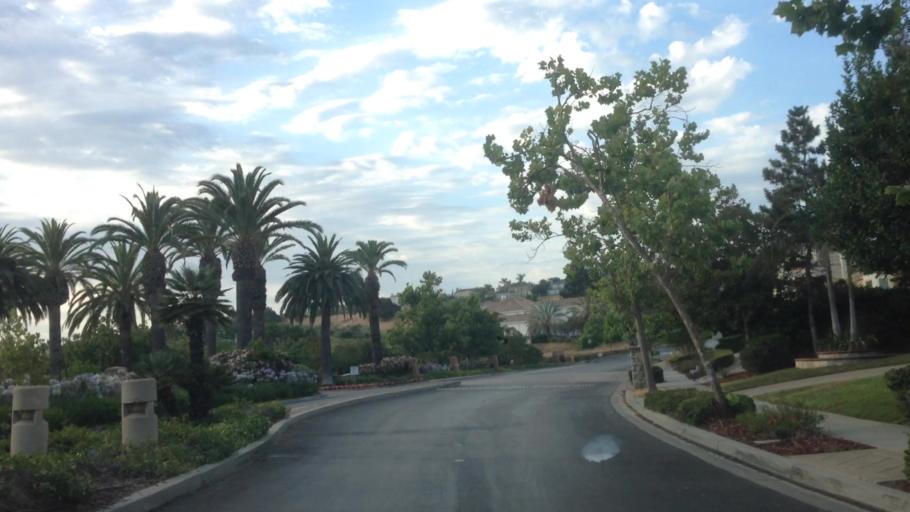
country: US
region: California
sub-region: Santa Clara County
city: Seven Trees
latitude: 37.2756
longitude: -121.7730
